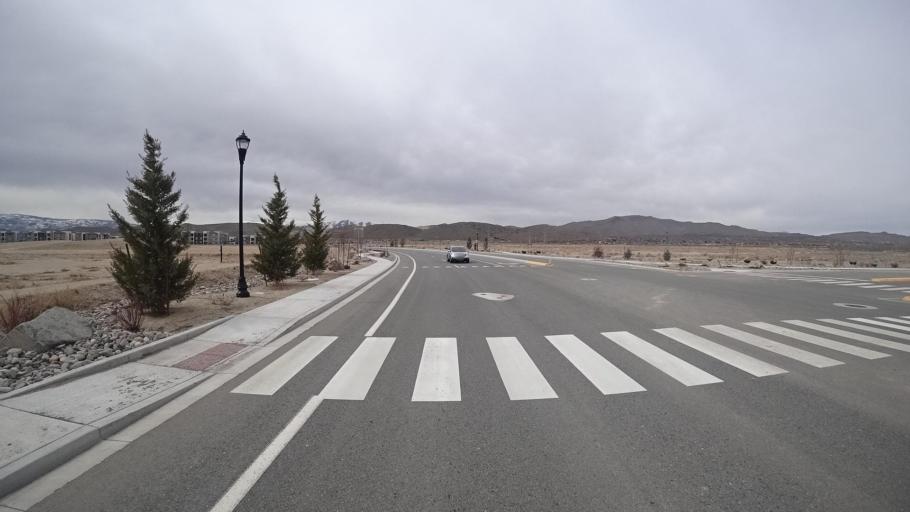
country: US
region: Nevada
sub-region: Washoe County
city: Spanish Springs
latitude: 39.6158
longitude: -119.7073
